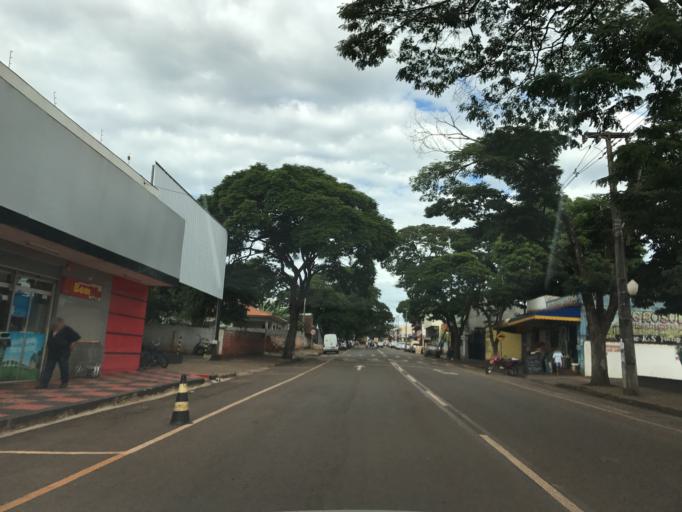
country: BR
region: Parana
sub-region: Sarandi
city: Sarandi
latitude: -23.4339
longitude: -51.8688
